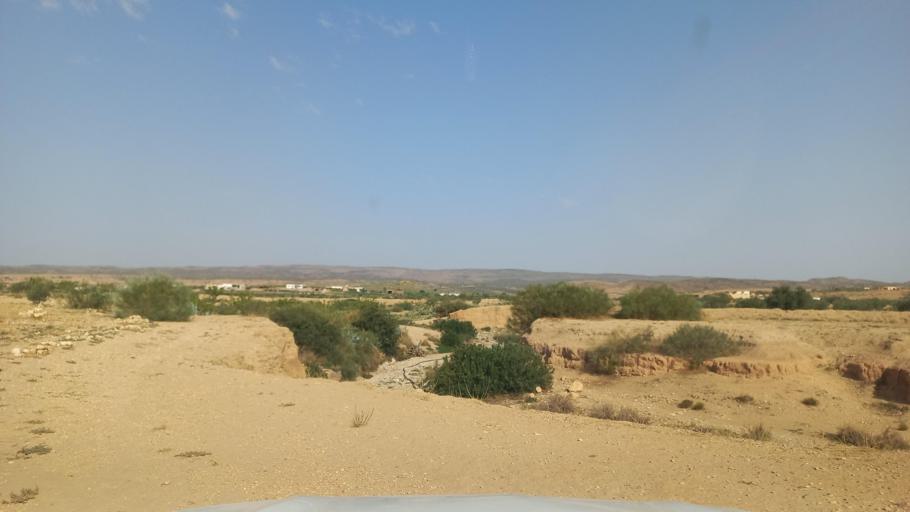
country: TN
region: Al Qasrayn
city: Kasserine
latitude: 35.2961
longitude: 8.9668
